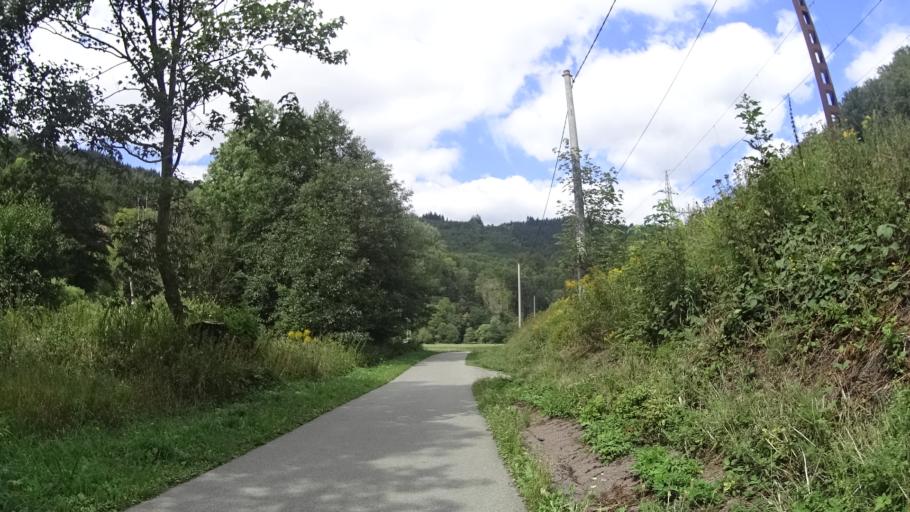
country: CZ
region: Pardubicky
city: Horni Sloupnice
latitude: 49.9744
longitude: 16.3385
